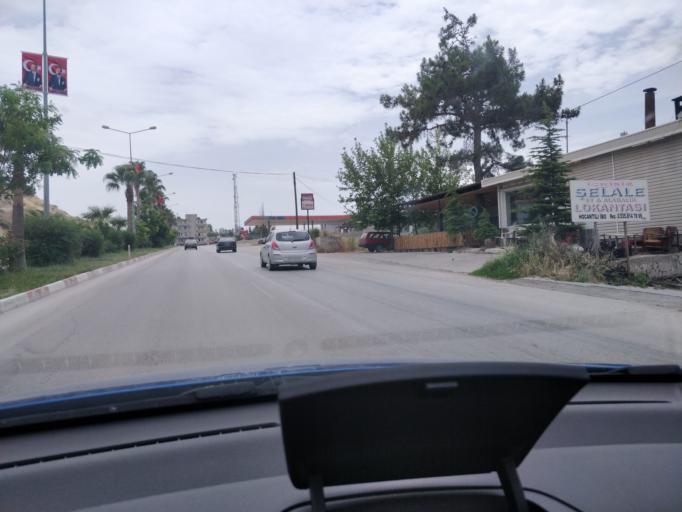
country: TR
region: Mersin
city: Mut
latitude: 36.6486
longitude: 33.4270
